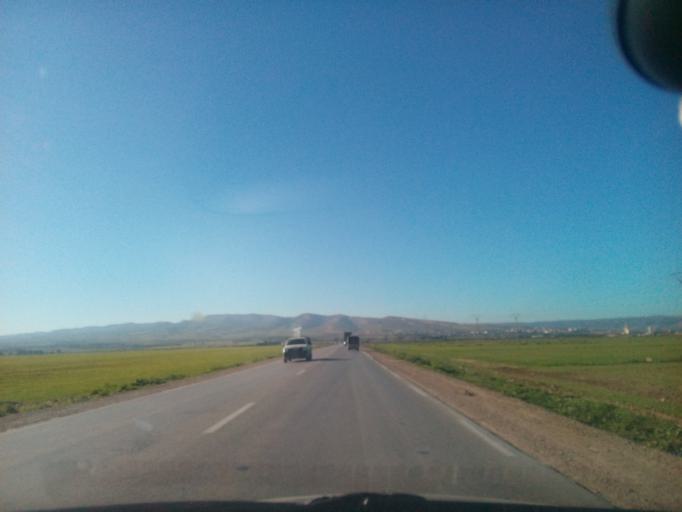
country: DZ
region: Relizane
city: Relizane
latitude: 35.8977
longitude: 0.5567
